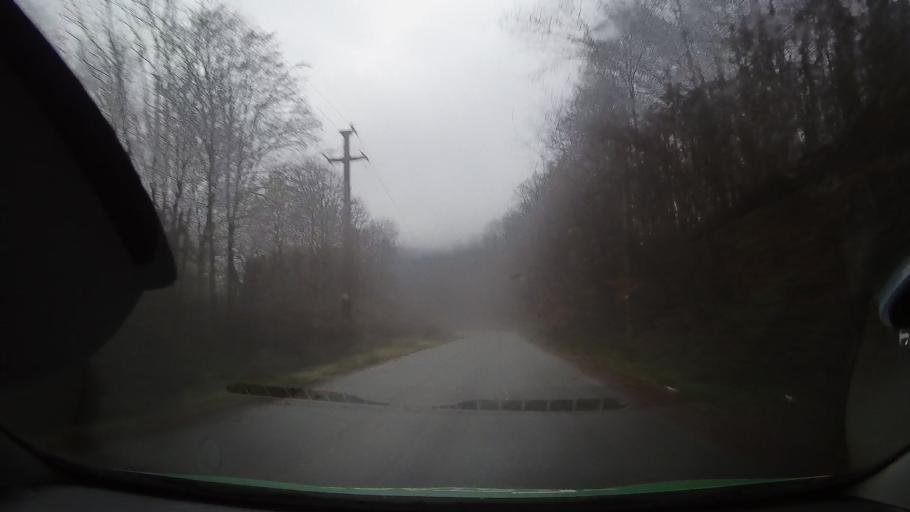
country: RO
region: Hunedoara
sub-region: Comuna Ribita
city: Ribita
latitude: 46.2468
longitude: 22.7501
